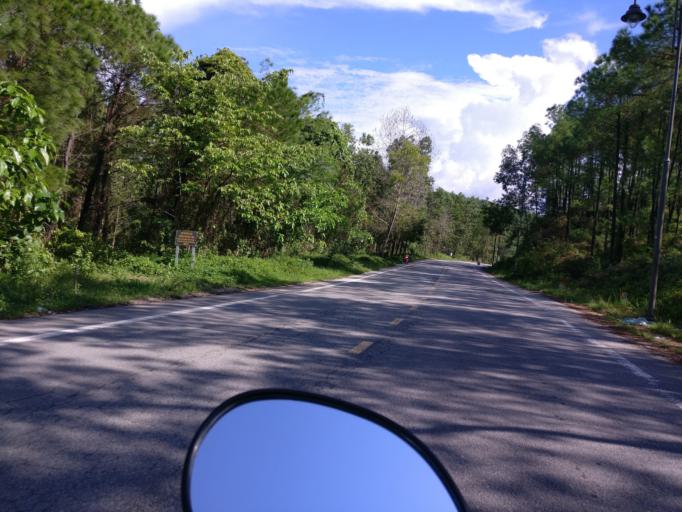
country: VN
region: Thua Thien-Hue
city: Hue
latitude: 16.4042
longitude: 107.5897
